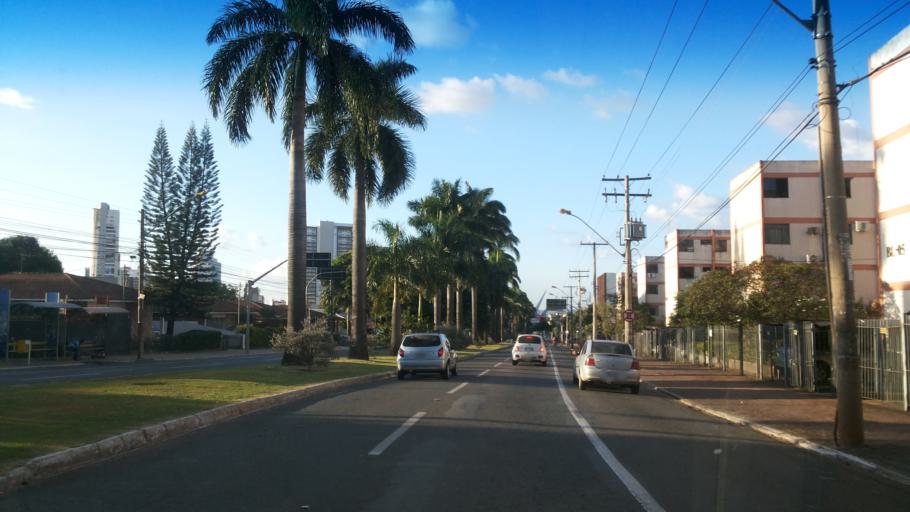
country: BR
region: Goias
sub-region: Goiania
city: Goiania
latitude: -16.6959
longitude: -49.2643
